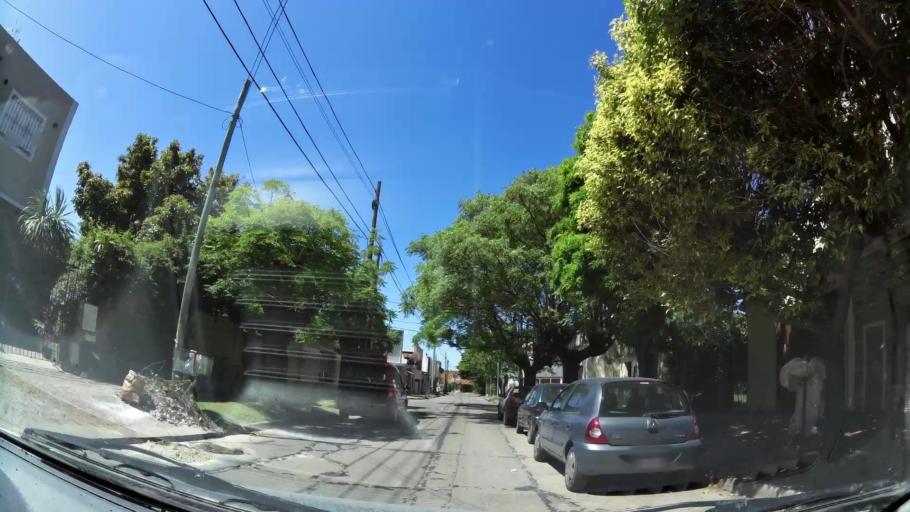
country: AR
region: Buenos Aires
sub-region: Partido de Quilmes
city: Quilmes
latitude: -34.7160
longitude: -58.2855
